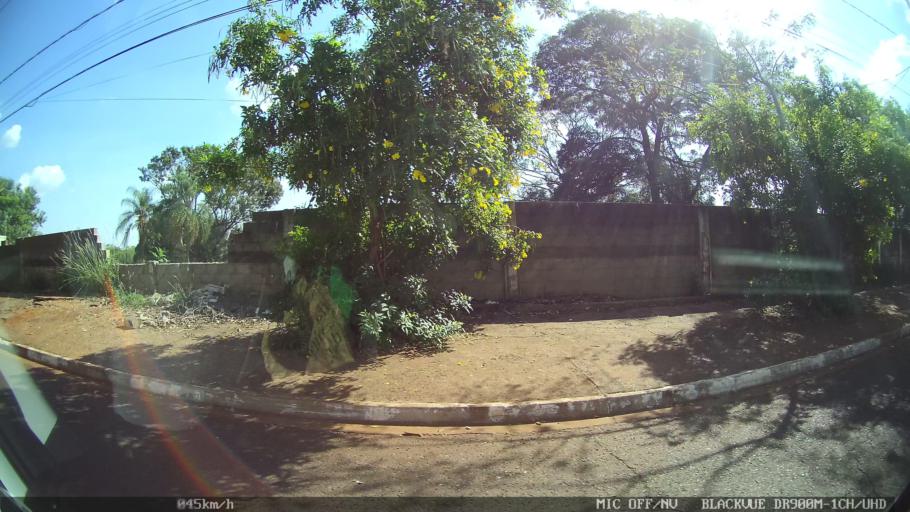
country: BR
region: Sao Paulo
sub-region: Ribeirao Preto
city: Ribeirao Preto
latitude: -21.1878
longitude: -47.8440
